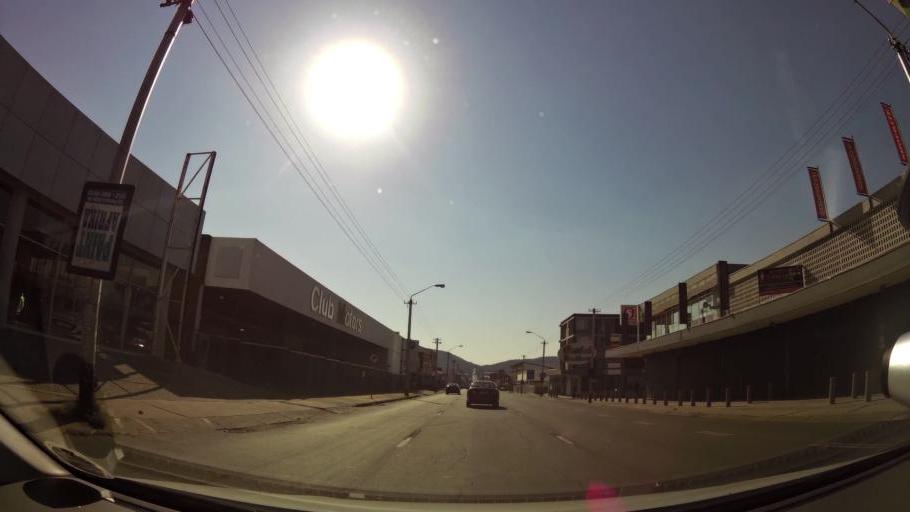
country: ZA
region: Gauteng
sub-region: City of Tshwane Metropolitan Municipality
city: Pretoria
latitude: -25.7135
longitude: 28.2016
